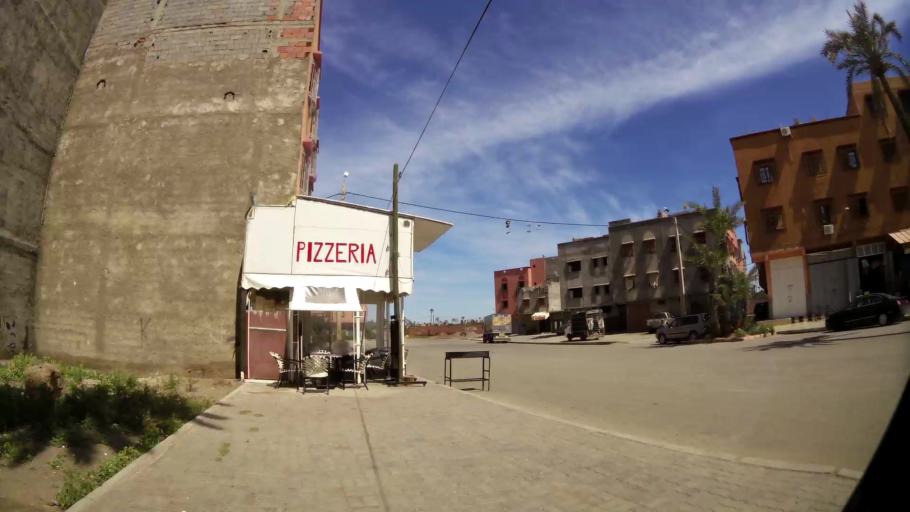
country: MA
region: Marrakech-Tensift-Al Haouz
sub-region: Marrakech
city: Marrakesh
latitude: 31.6631
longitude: -7.9841
